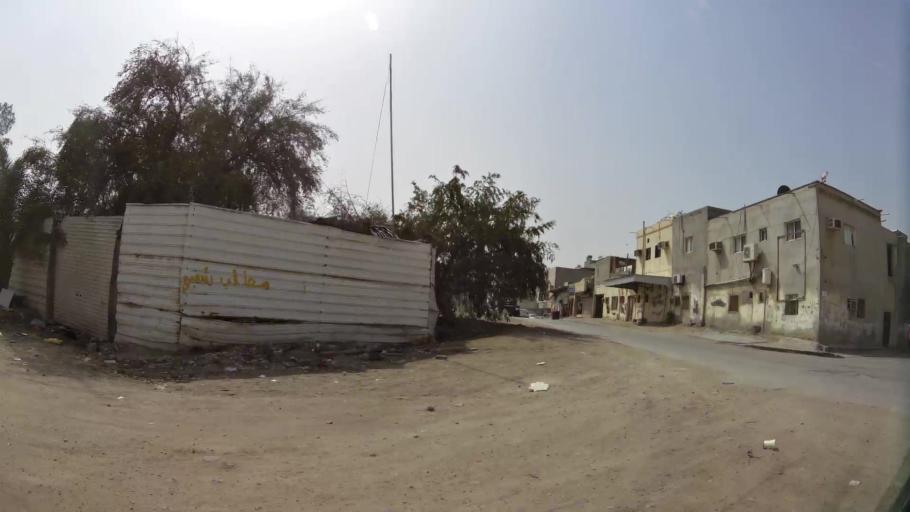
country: BH
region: Manama
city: Jidd Hafs
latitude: 26.2224
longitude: 50.5173
